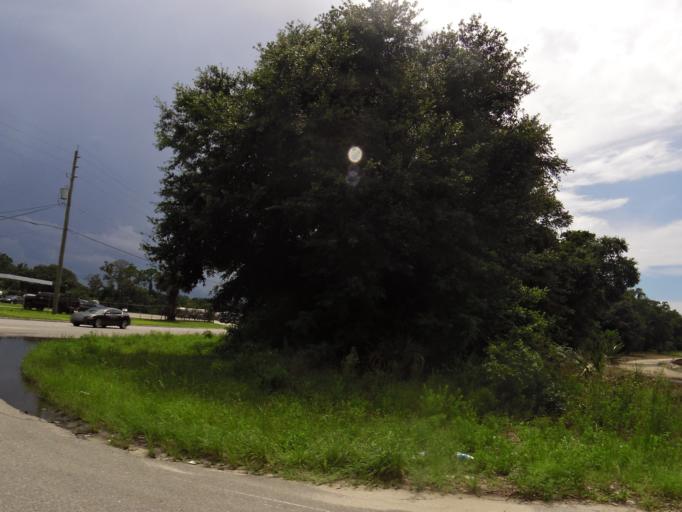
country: US
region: Florida
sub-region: Duval County
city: Jacksonville
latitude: 30.3768
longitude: -81.6412
